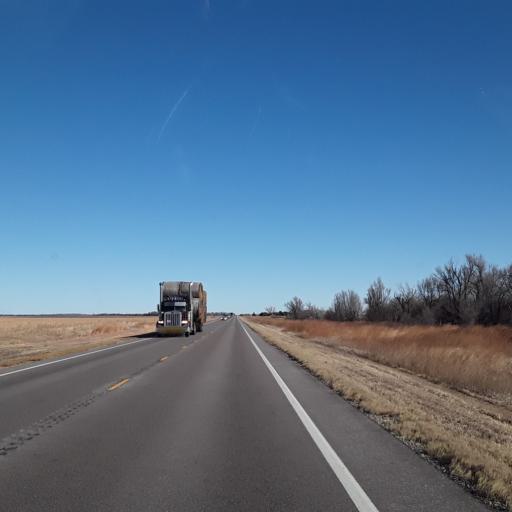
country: US
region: Kansas
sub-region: Pawnee County
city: Larned
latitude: 38.0970
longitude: -99.2123
